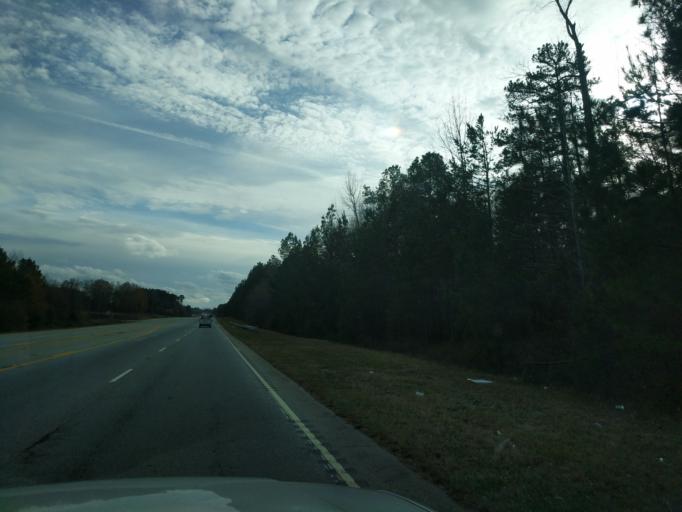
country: US
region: South Carolina
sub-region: Anderson County
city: Honea Path
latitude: 34.5458
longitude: -82.3169
